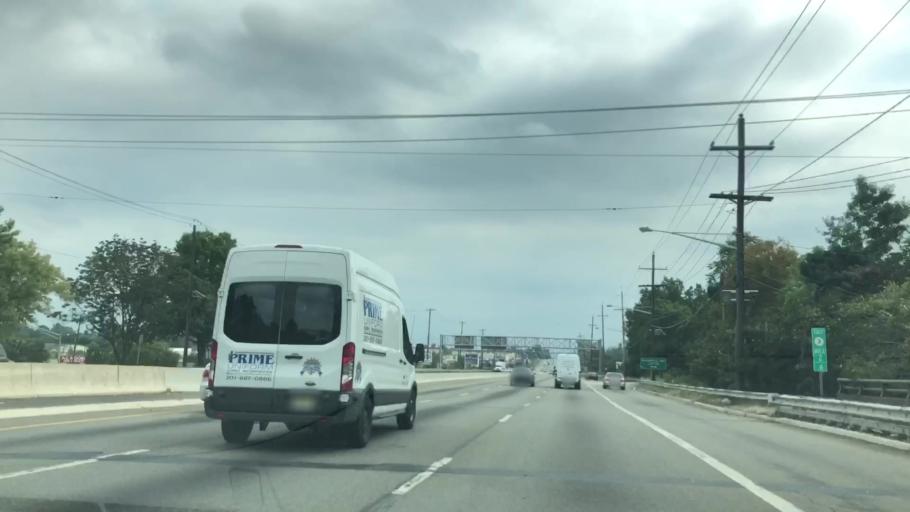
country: US
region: New Jersey
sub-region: Essex County
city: Nutley
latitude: 40.8403
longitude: -74.1614
